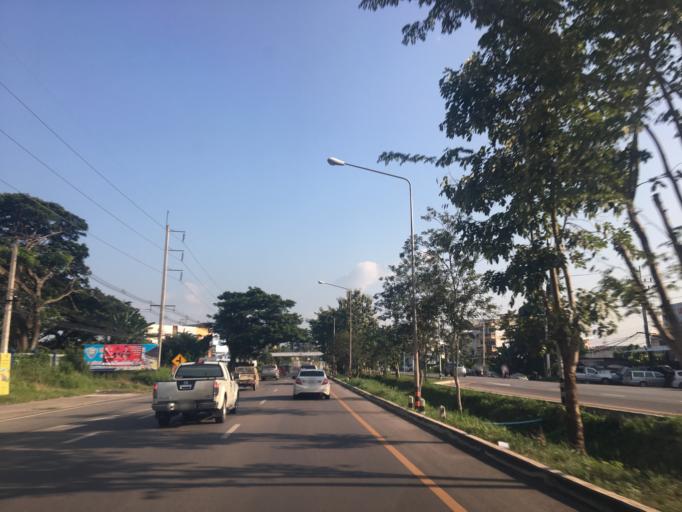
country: TH
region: Phayao
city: Phayao
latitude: 19.1656
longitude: 99.9111
